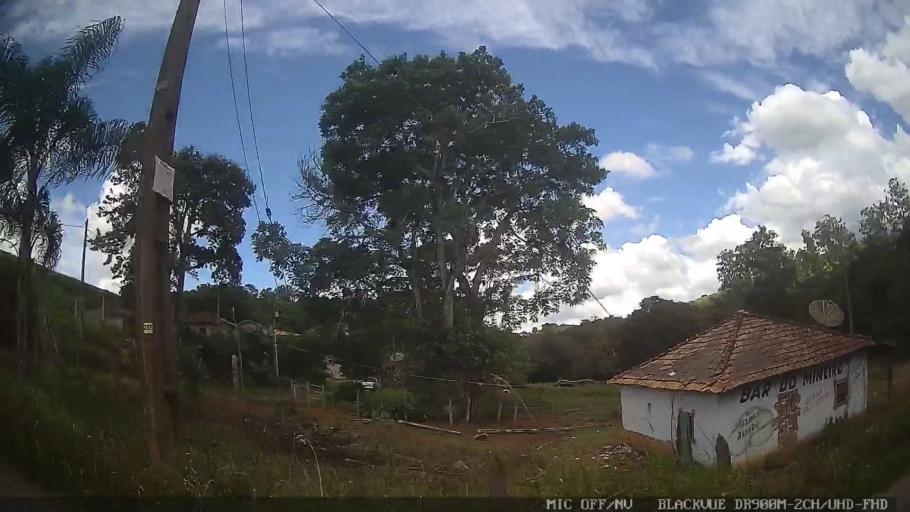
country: BR
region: Minas Gerais
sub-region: Extrema
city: Extrema
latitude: -22.7350
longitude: -46.4266
